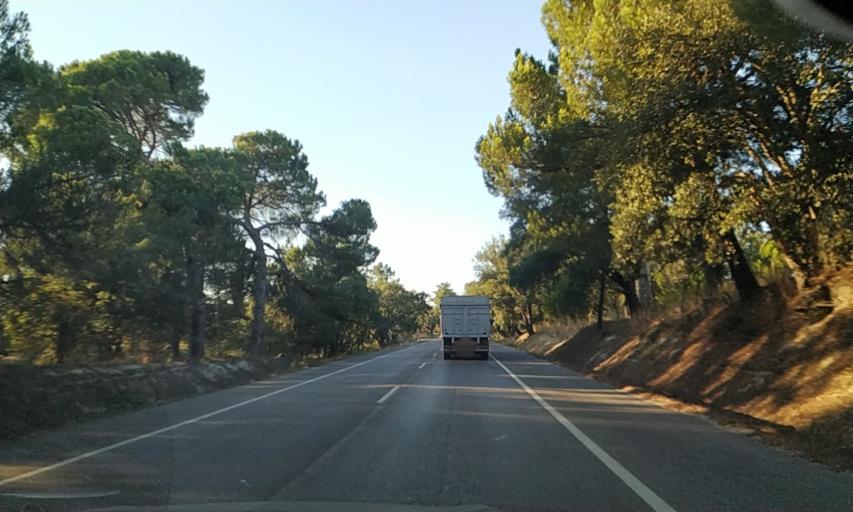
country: PT
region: Setubal
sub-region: Alcacer do Sal
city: Alcacer do Sal
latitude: 38.5496
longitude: -8.6491
